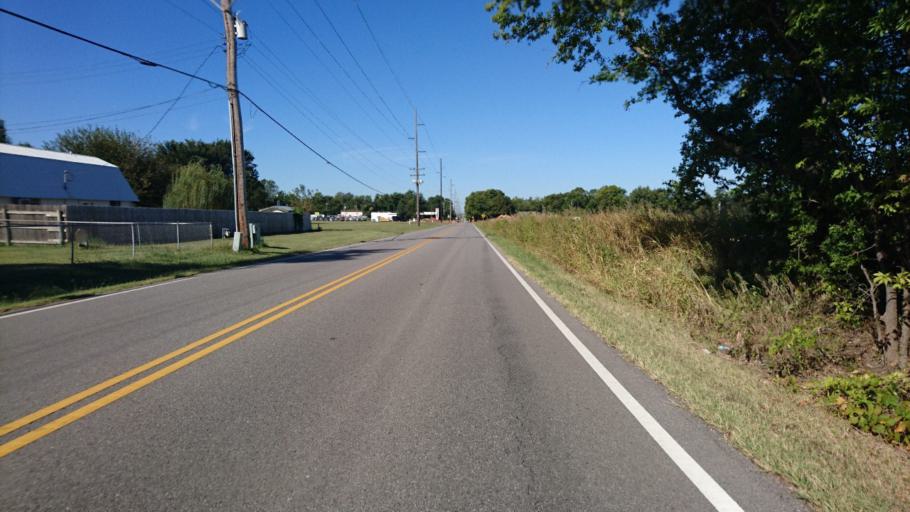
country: US
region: Oklahoma
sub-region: Rogers County
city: Catoosa
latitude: 36.1480
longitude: -95.8120
